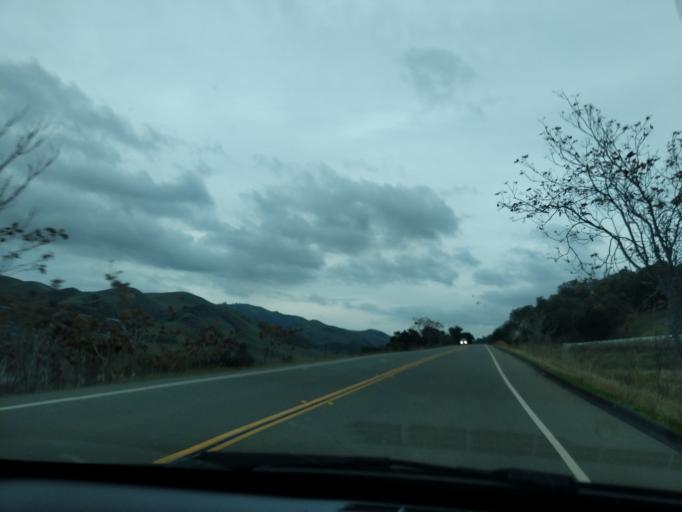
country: US
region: California
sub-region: Monterey County
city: Soledad
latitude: 36.6130
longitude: -121.2079
